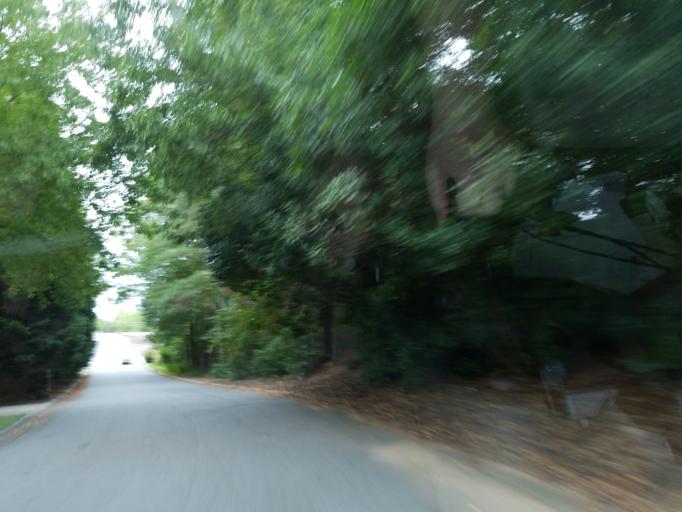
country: US
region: Georgia
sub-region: Fulton County
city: Sandy Springs
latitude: 33.9704
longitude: -84.4173
